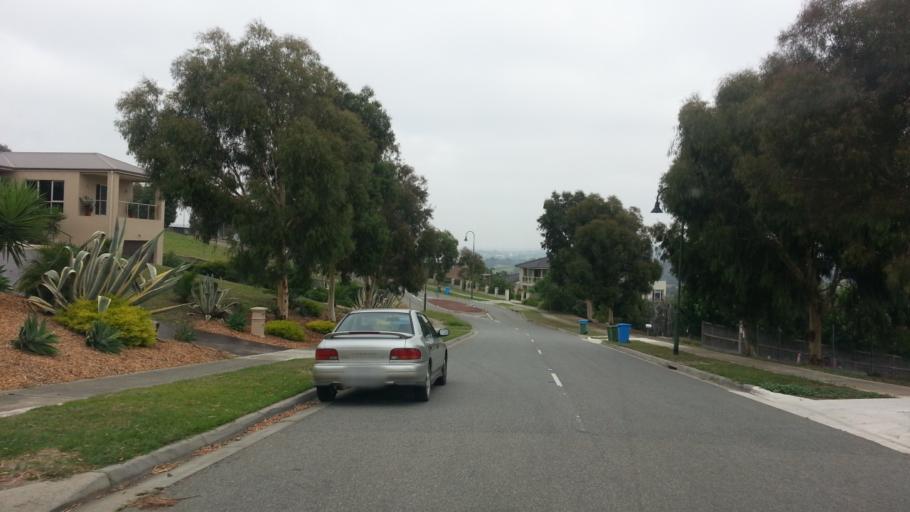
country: AU
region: Victoria
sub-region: Casey
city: Narre Warren North
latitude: -37.9963
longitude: 145.3292
